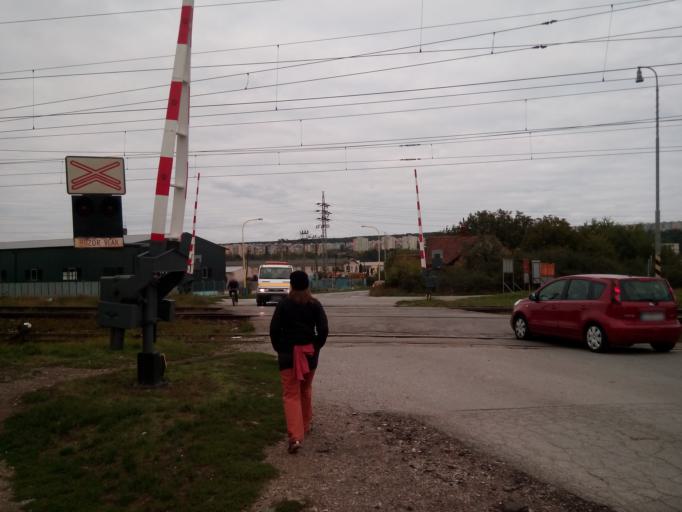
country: SK
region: Kosicky
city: Kosice
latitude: 48.7341
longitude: 21.2628
